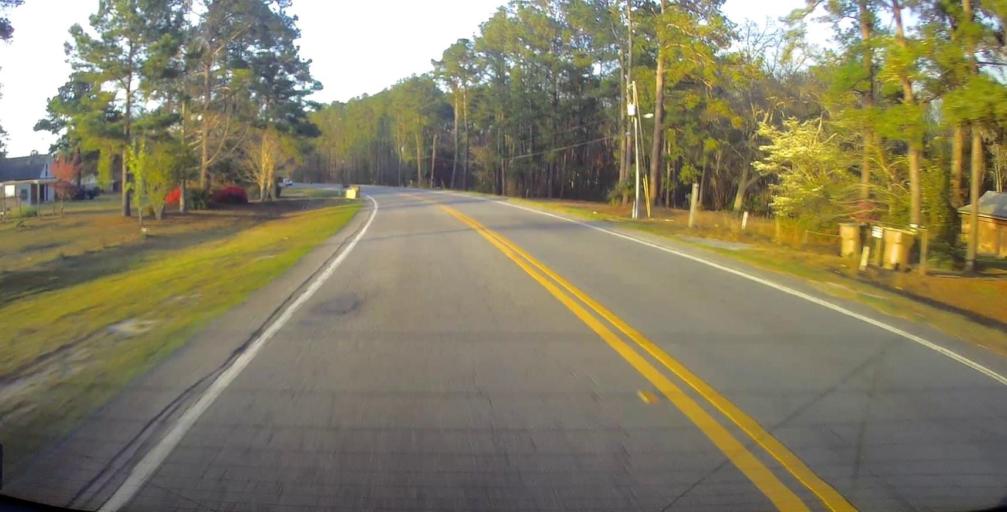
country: US
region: Georgia
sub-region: Chatham County
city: Bloomingdale
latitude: 32.1638
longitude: -81.3850
